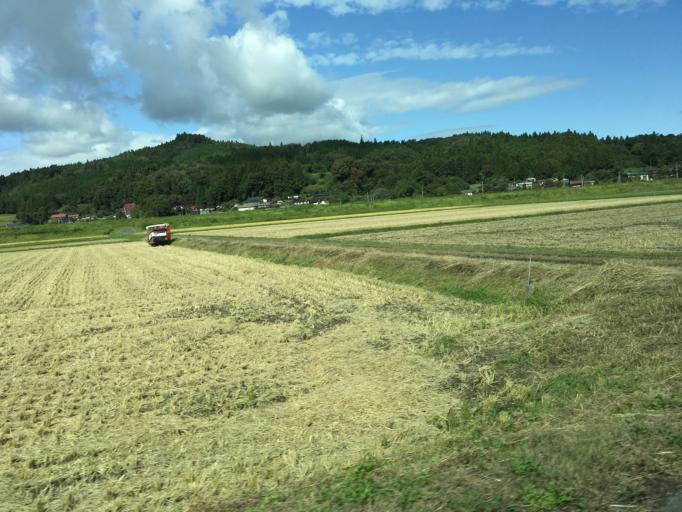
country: JP
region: Iwate
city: Ichinoseki
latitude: 38.8448
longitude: 141.2758
